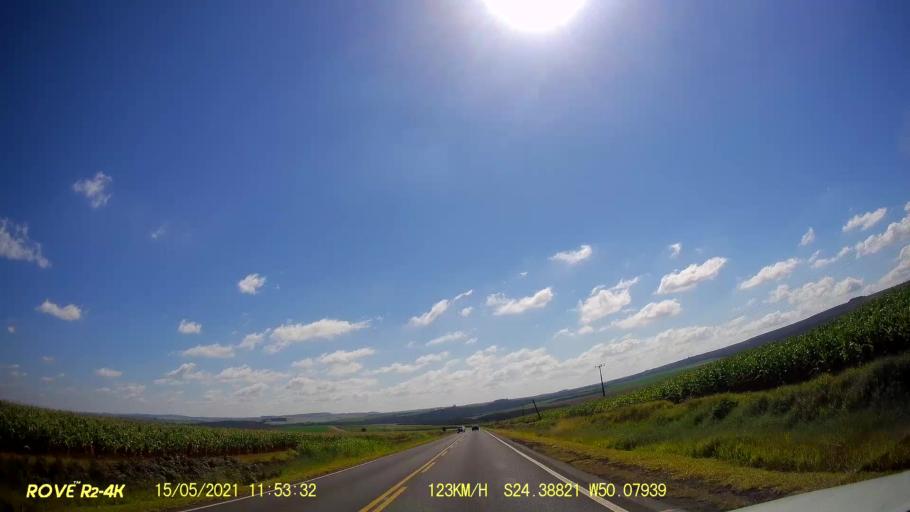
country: BR
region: Parana
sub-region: Pirai Do Sul
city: Pirai do Sul
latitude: -24.3891
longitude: -50.0792
